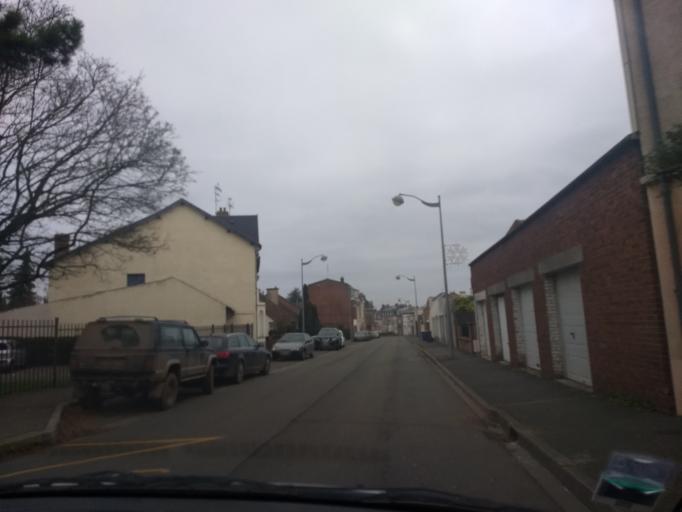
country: FR
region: Nord-Pas-de-Calais
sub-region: Departement du Pas-de-Calais
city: Arras
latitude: 50.2821
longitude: 2.7876
